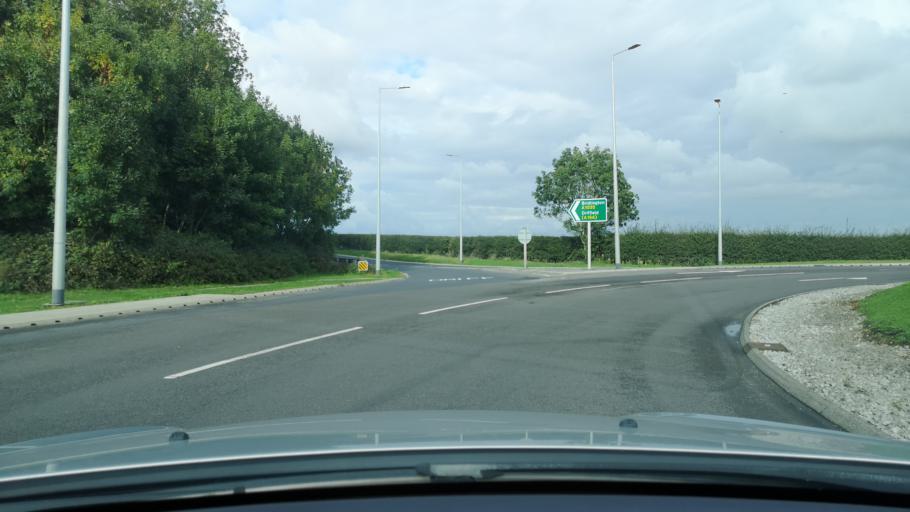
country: GB
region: England
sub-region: East Riding of Yorkshire
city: Walkington
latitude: 53.8431
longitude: -0.4781
